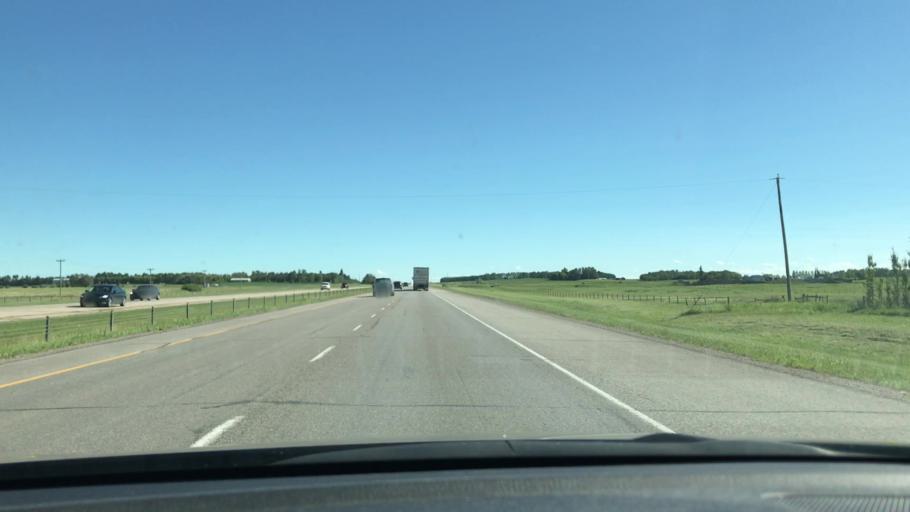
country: CA
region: Alberta
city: Olds
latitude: 51.8959
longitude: -114.0249
